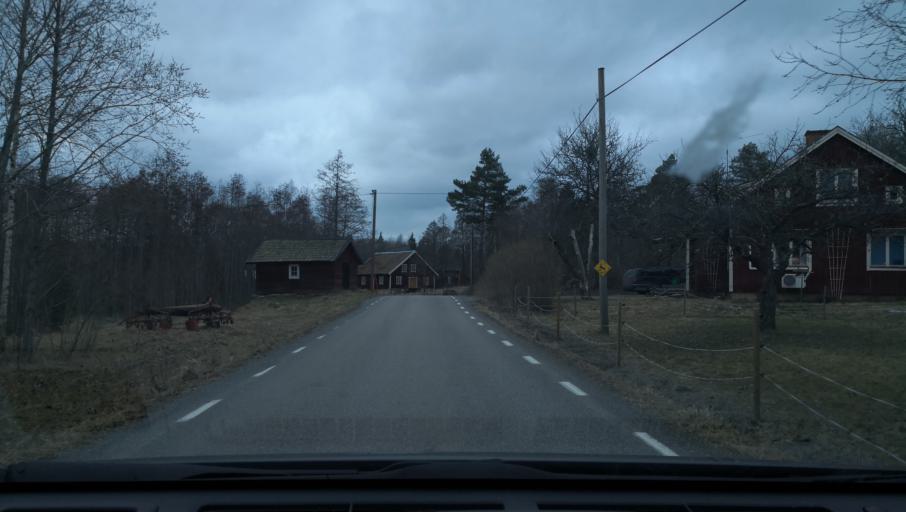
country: SE
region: Vaestmanland
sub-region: Kopings Kommun
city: Kolsva
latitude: 59.5672
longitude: 15.7315
